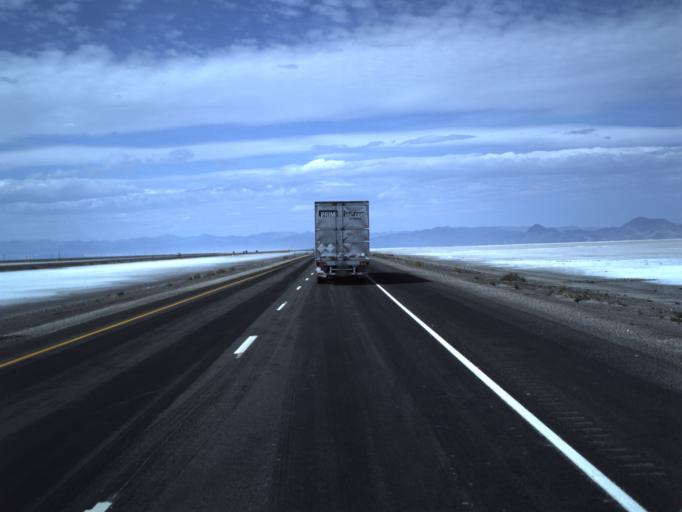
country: US
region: Utah
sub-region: Tooele County
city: Wendover
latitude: 40.7355
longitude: -113.6649
